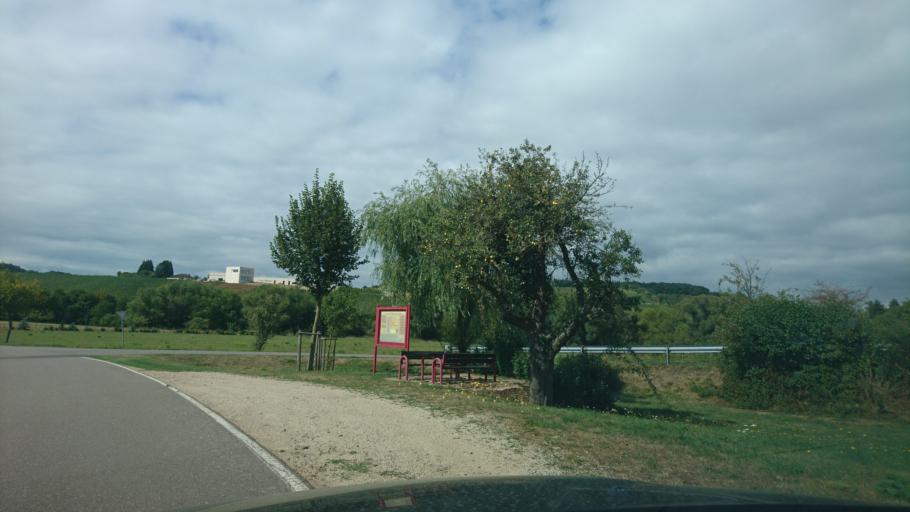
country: DE
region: Rheinland-Pfalz
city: Schoden
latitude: 49.6396
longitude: 6.5846
